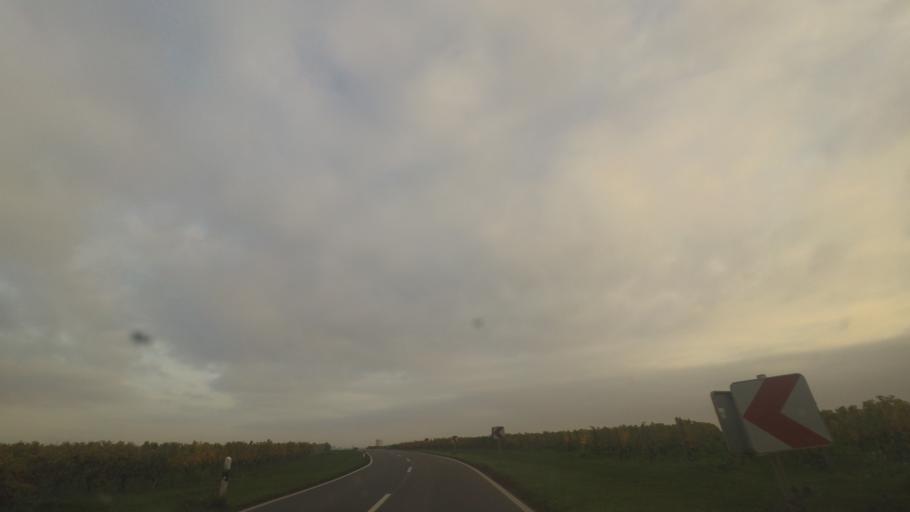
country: DE
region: Rheinland-Pfalz
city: Bechtheim
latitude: 49.7142
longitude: 8.3069
